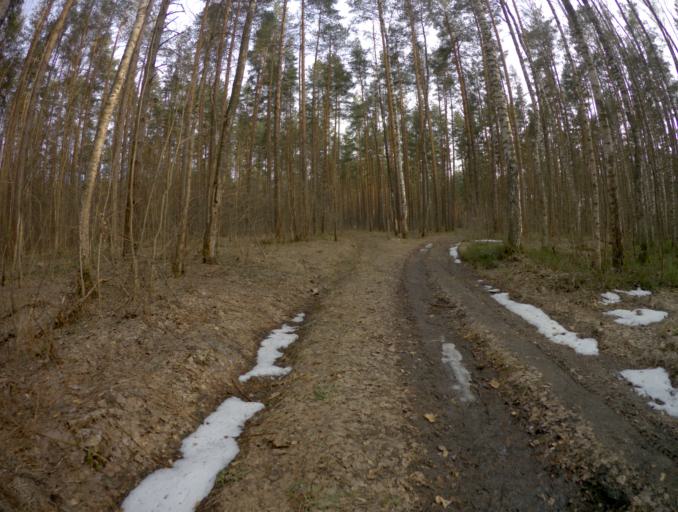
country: RU
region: Vladimir
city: Kommunar
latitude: 56.0738
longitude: 40.4402
